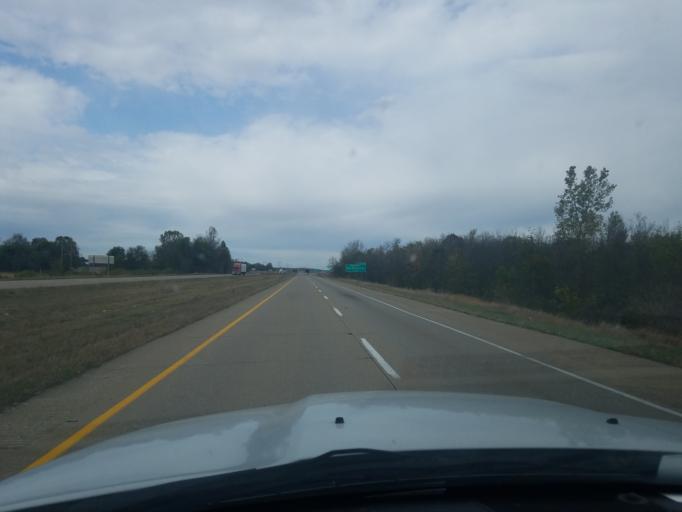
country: US
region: Indiana
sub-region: Vanderburgh County
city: Melody Hill
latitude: 38.0737
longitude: -87.4760
